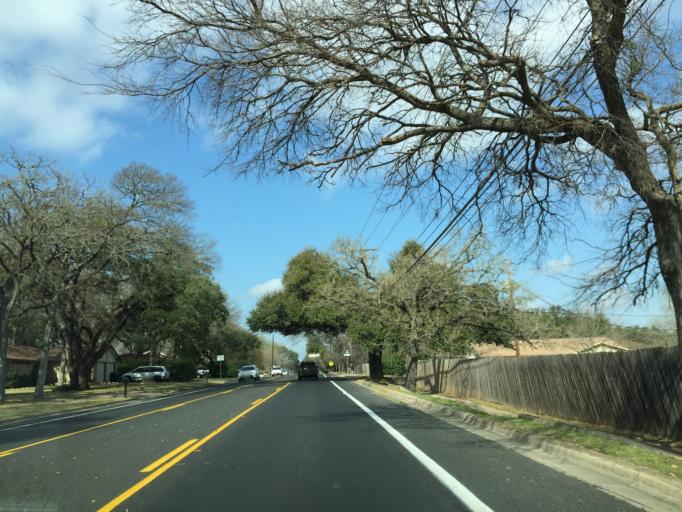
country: US
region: Texas
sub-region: Williamson County
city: Jollyville
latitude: 30.4160
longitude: -97.7388
